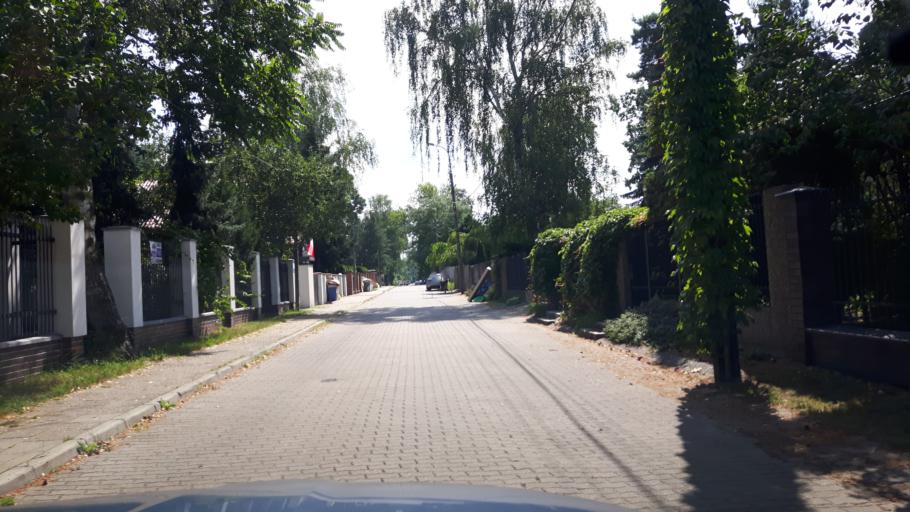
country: PL
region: Masovian Voivodeship
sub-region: Warszawa
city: Wawer
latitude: 52.2222
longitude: 21.1607
